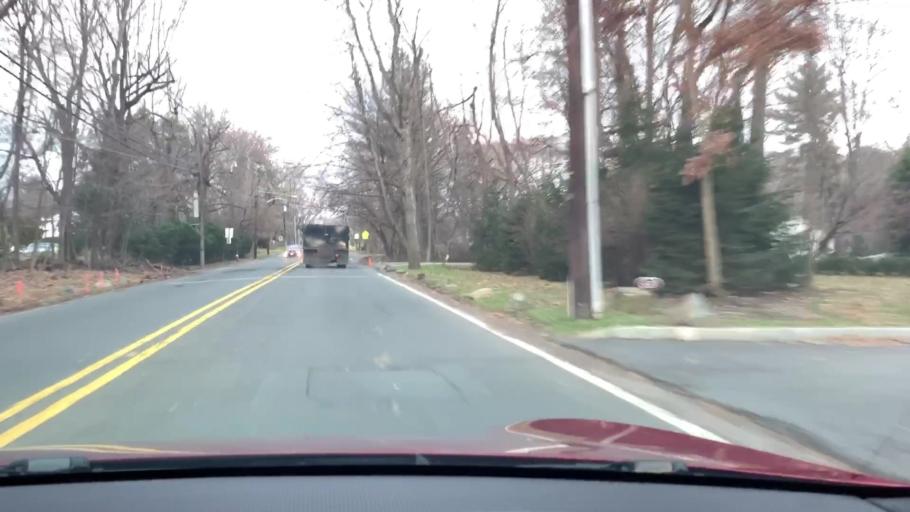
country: US
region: New Jersey
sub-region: Bergen County
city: Tenafly
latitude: 40.9146
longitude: -73.9798
